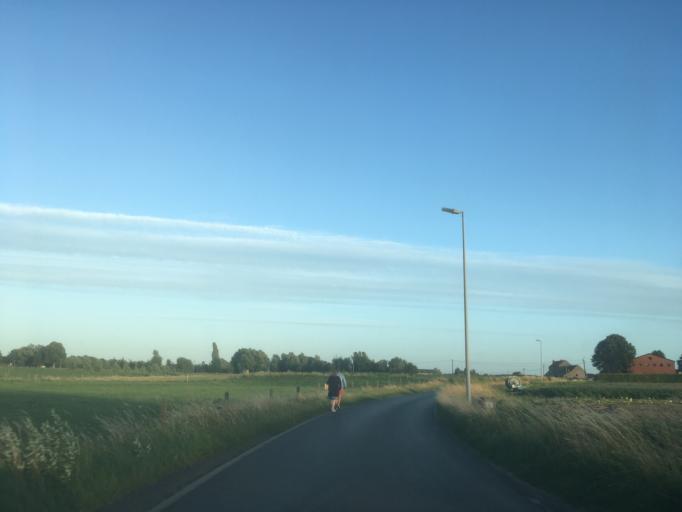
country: BE
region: Flanders
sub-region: Provincie West-Vlaanderen
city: Torhout
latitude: 51.0373
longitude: 3.0925
